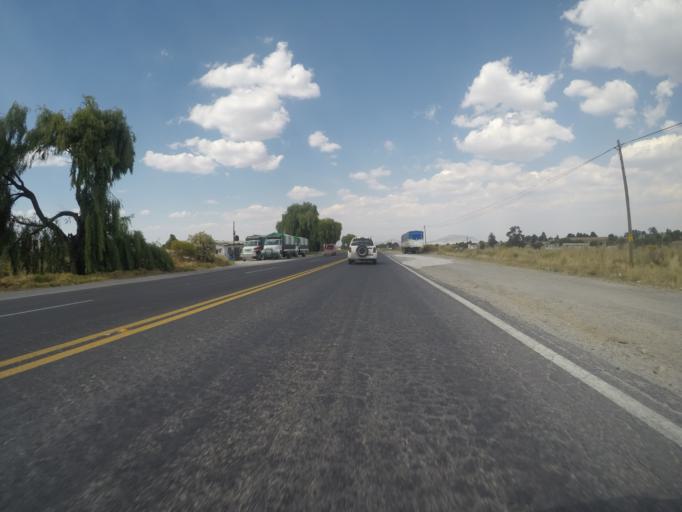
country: MX
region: Mexico
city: San Juan de las Huertas
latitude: 19.2369
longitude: -99.7744
